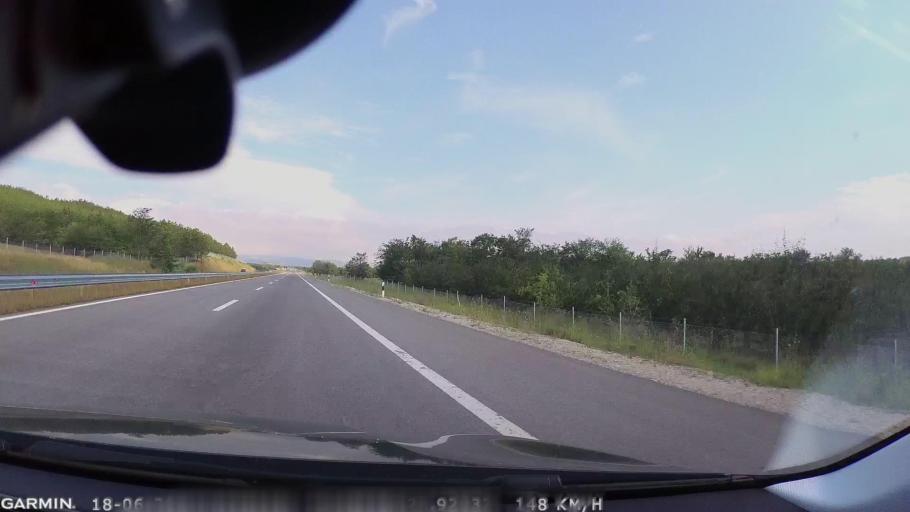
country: MK
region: Sveti Nikole
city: Sveti Nikole
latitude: 41.8984
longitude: 21.9185
